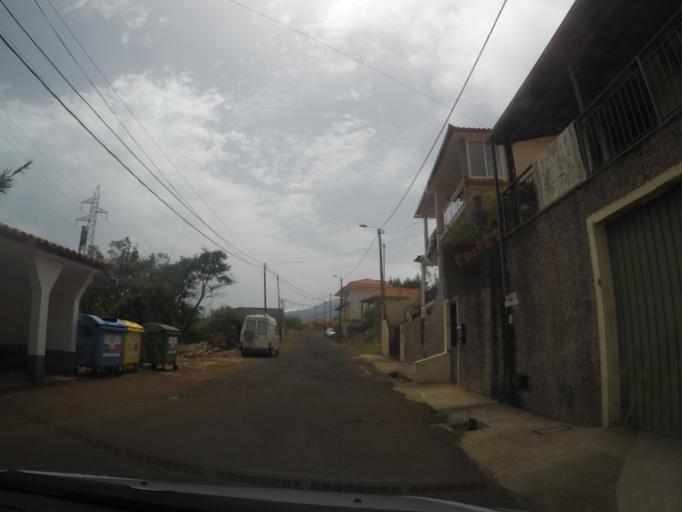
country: PT
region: Madeira
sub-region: Santa Cruz
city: Santa Cruz
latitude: 32.7024
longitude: -16.7902
